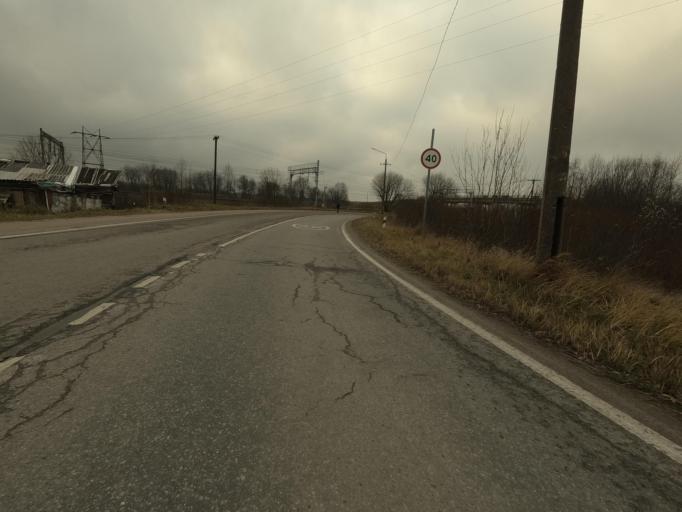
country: RU
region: Leningrad
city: Lyuban'
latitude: 59.4869
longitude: 31.2672
